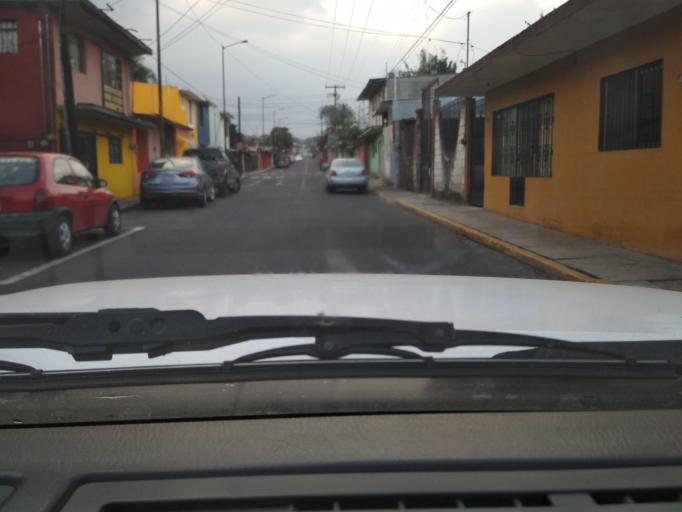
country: MX
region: Veracruz
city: Orizaba
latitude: 18.8670
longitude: -97.1014
